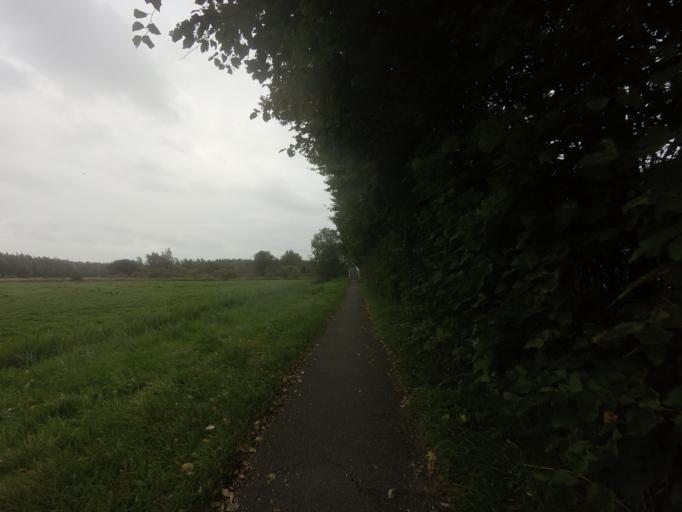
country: NL
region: Friesland
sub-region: Gemeente Leeuwarden
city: Bilgaard
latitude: 53.2262
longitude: 5.7926
